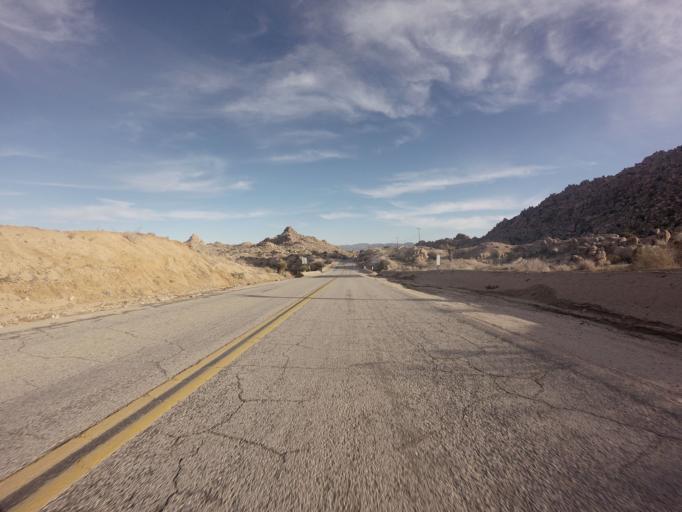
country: US
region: California
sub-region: San Bernardino County
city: Yucca Valley
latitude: 34.1479
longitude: -116.4809
